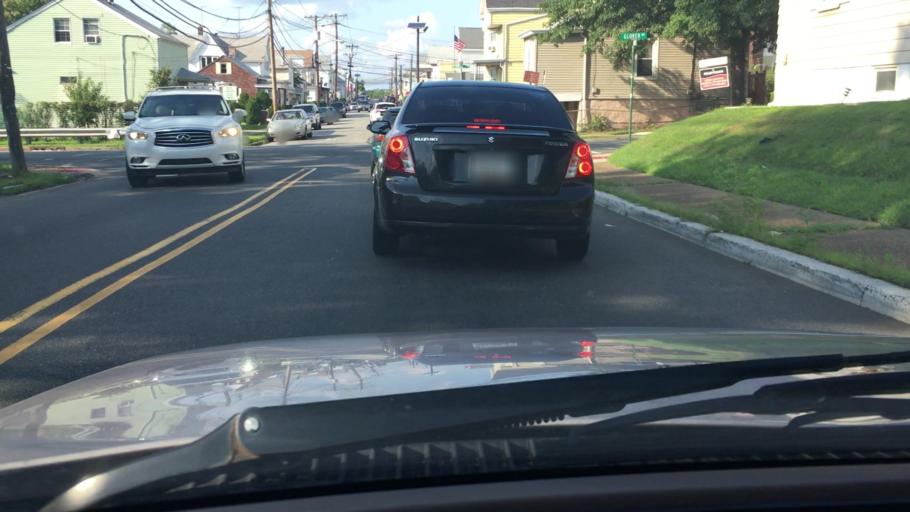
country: US
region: New Jersey
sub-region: Passaic County
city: Woodland Park
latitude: 40.9062
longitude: -74.1920
